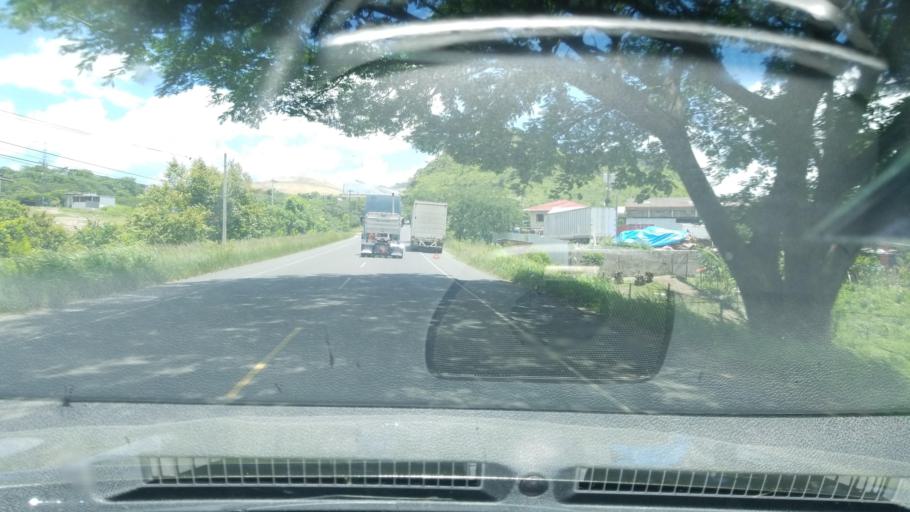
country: HN
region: Francisco Morazan
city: Rio Abajo
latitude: 14.1504
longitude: -87.2094
